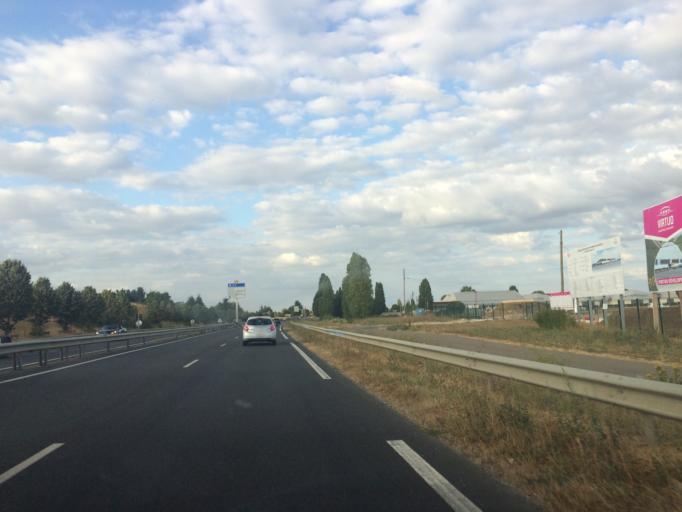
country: FR
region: Ile-de-France
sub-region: Departement de l'Essonne
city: Le Plessis-Pate
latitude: 48.6000
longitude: 2.3160
